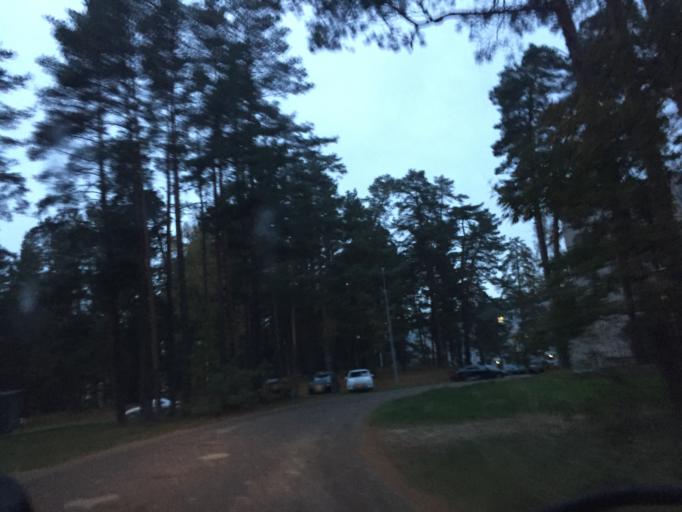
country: LV
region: Adazi
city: Adazi
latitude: 57.0901
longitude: 24.3615
